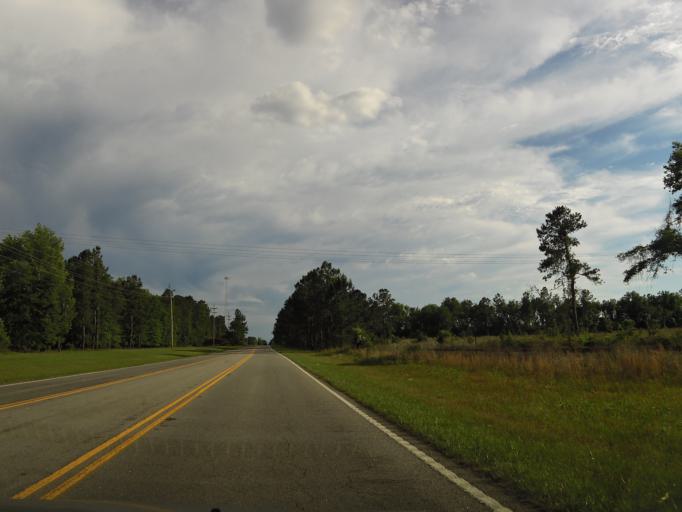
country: US
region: South Carolina
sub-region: Hampton County
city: Estill
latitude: 32.7851
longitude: -81.2406
